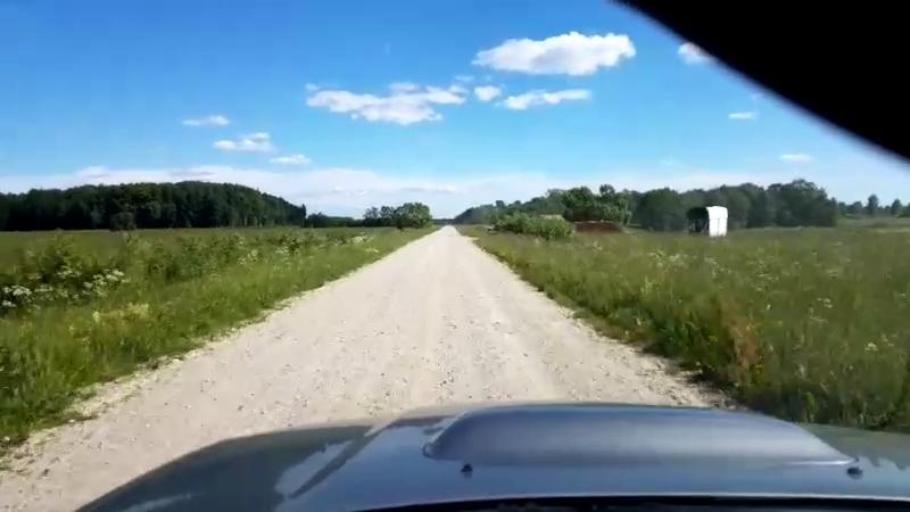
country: EE
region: Paernumaa
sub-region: Sauga vald
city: Sauga
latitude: 58.5080
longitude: 24.5178
